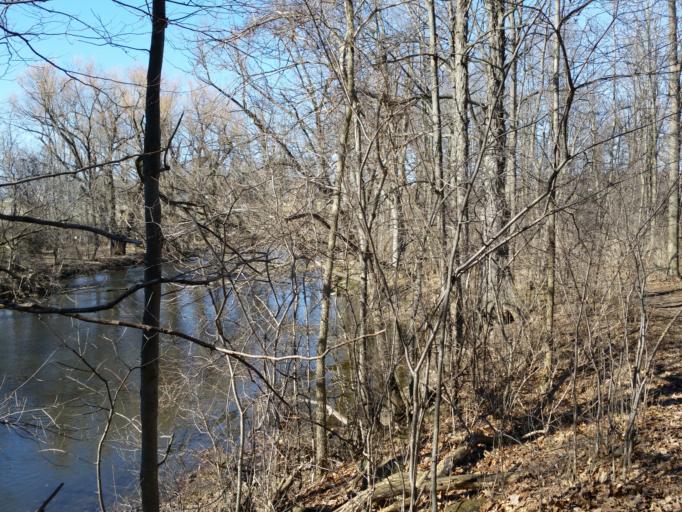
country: US
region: New York
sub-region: Monroe County
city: Churchville
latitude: 43.0866
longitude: -77.8043
